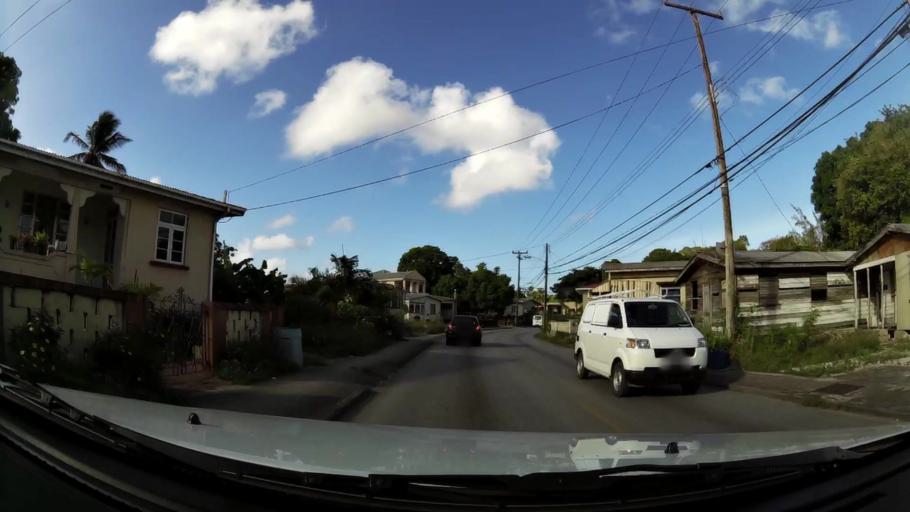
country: BB
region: Saint Michael
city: Bridgetown
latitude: 13.1030
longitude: -59.5899
